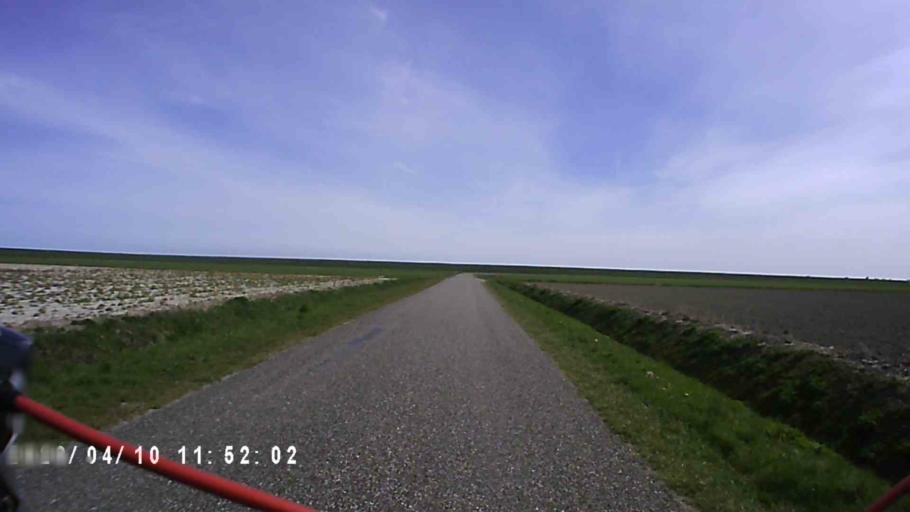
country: NL
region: Groningen
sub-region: Gemeente De Marne
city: Ulrum
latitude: 53.3936
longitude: 6.3279
